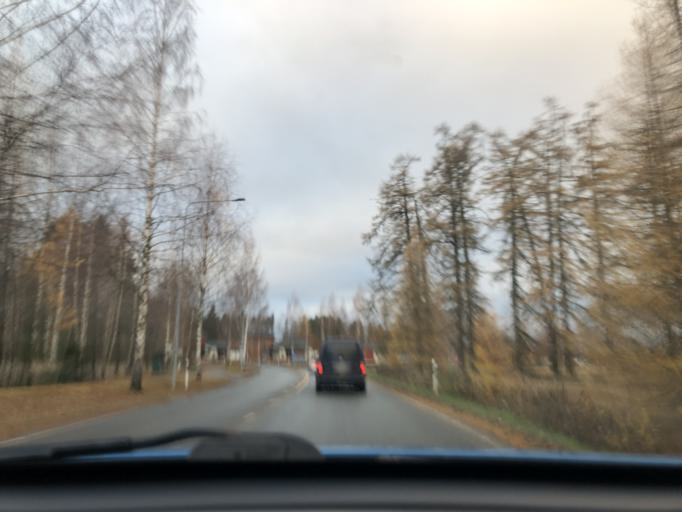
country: FI
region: Pirkanmaa
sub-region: Tampere
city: Kangasala
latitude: 61.4699
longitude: 24.0590
